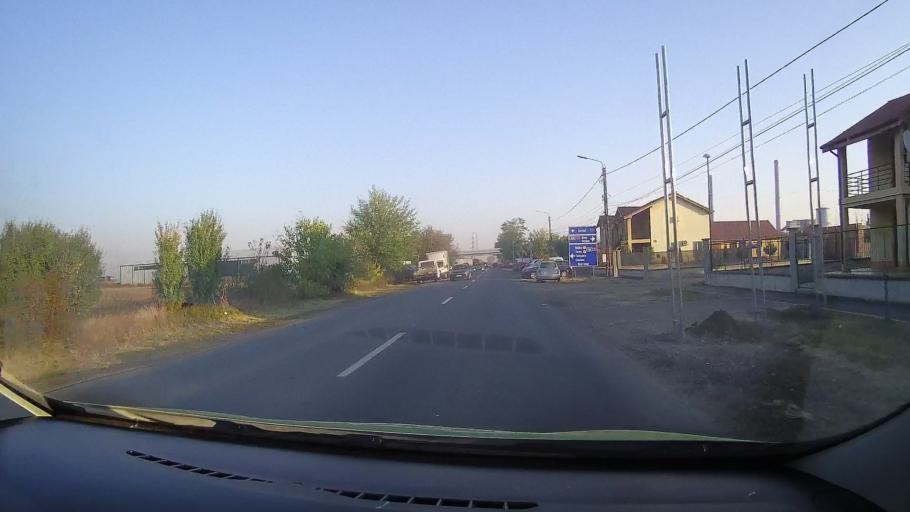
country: RO
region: Arad
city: Arad
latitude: 46.2146
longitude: 21.3206
